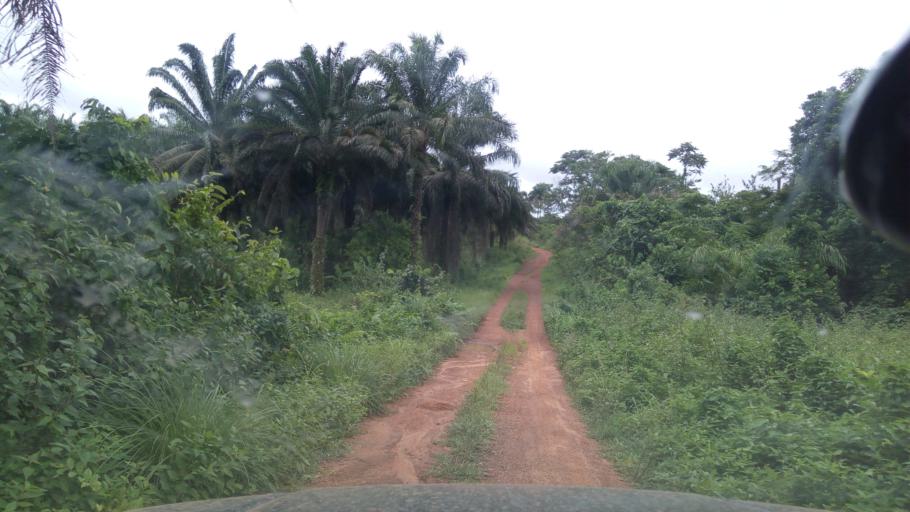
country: SL
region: Eastern Province
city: Gorahun
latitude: 7.6171
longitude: -11.2664
